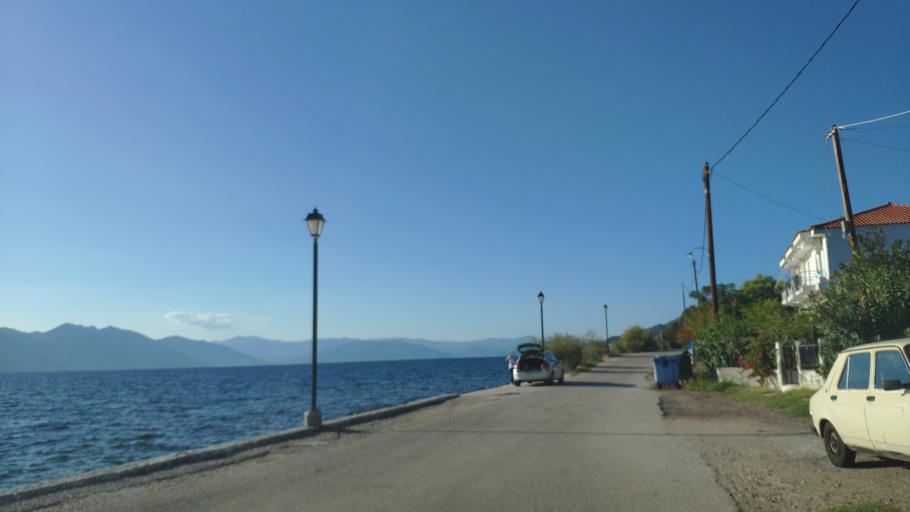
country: GR
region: Attica
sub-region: Nomos Piraios
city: Megalochori
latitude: 37.5911
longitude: 23.3403
